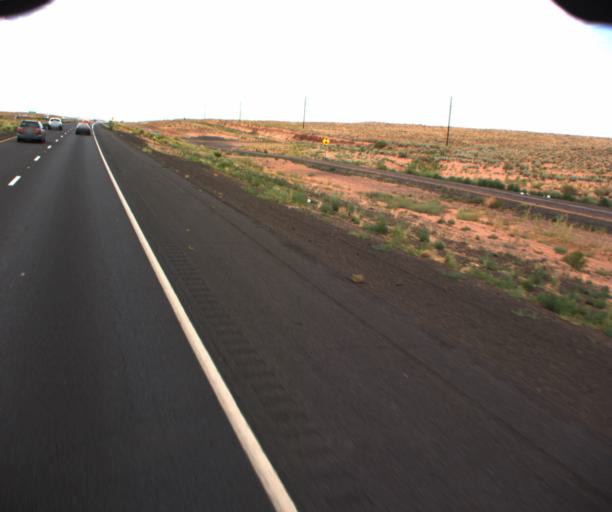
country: US
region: Arizona
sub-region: Navajo County
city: Winslow
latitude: 34.9750
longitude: -110.5228
